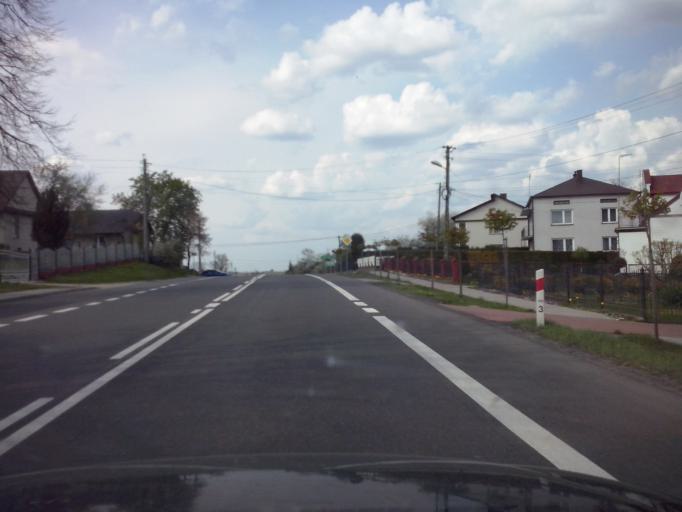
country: PL
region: Subcarpathian Voivodeship
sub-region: Powiat rzeszowski
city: Gorno
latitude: 50.3062
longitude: 22.1318
